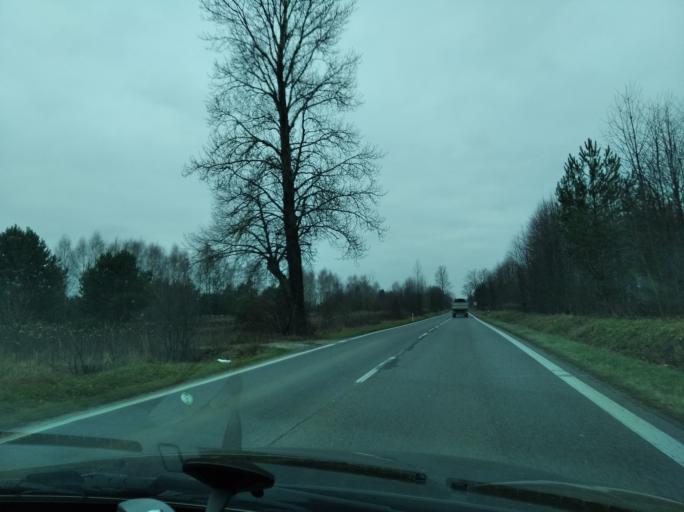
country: PL
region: Subcarpathian Voivodeship
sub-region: Powiat lancucki
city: Zolynia
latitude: 50.1551
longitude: 22.2902
